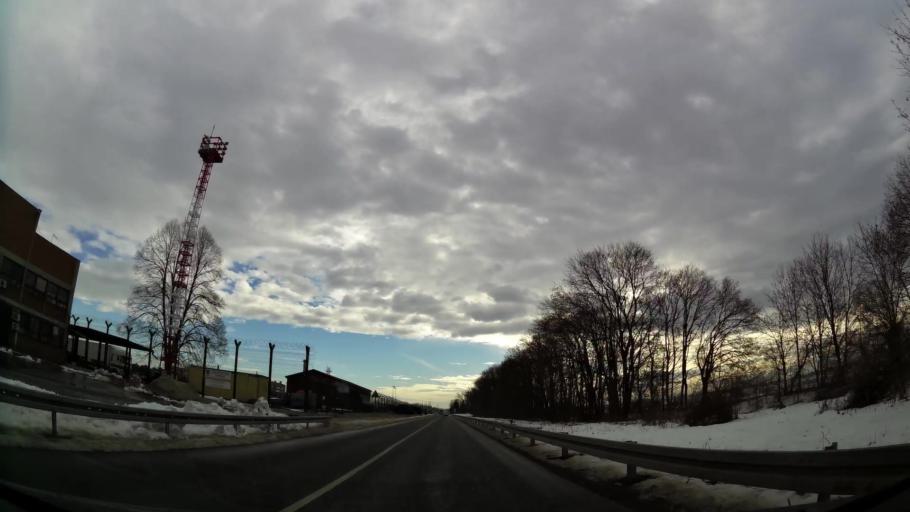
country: RS
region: Central Serbia
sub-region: Belgrade
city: Surcin
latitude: 44.8152
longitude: 20.2878
